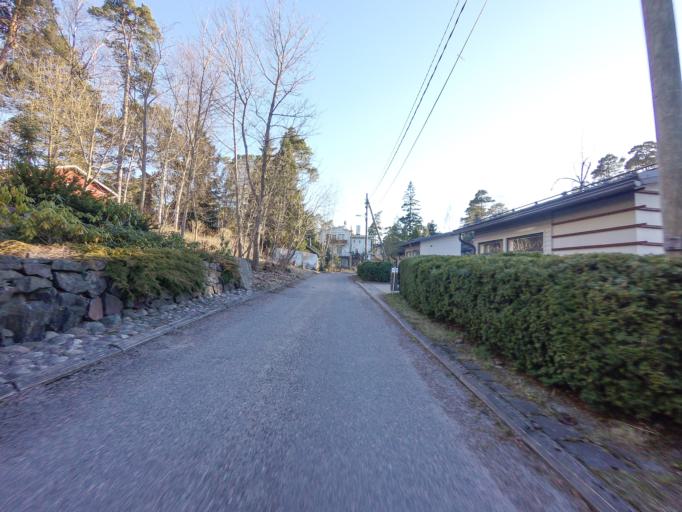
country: FI
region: Uusimaa
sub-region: Helsinki
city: Helsinki
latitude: 60.1762
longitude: 25.0217
